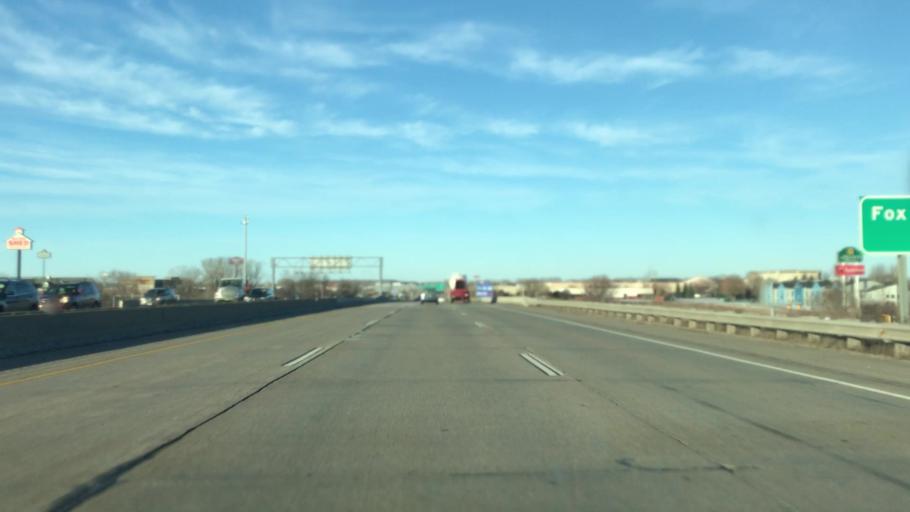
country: US
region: Wisconsin
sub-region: Outagamie County
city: Appleton
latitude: 44.2609
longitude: -88.4662
